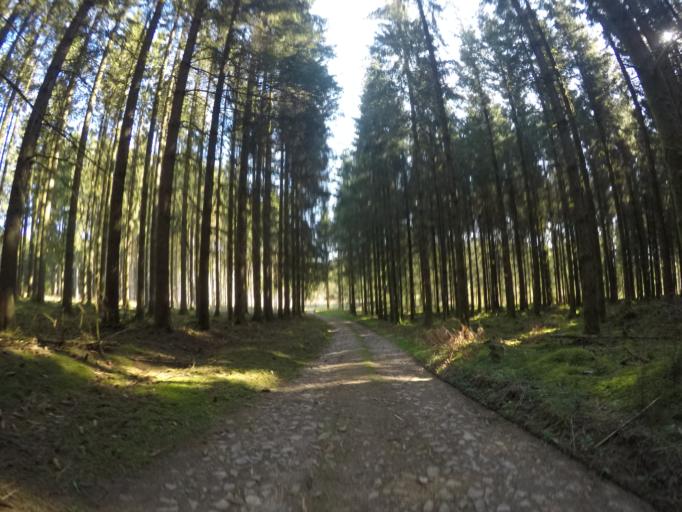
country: BE
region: Wallonia
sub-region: Province du Luxembourg
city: Leglise
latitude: 49.7844
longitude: 5.5872
